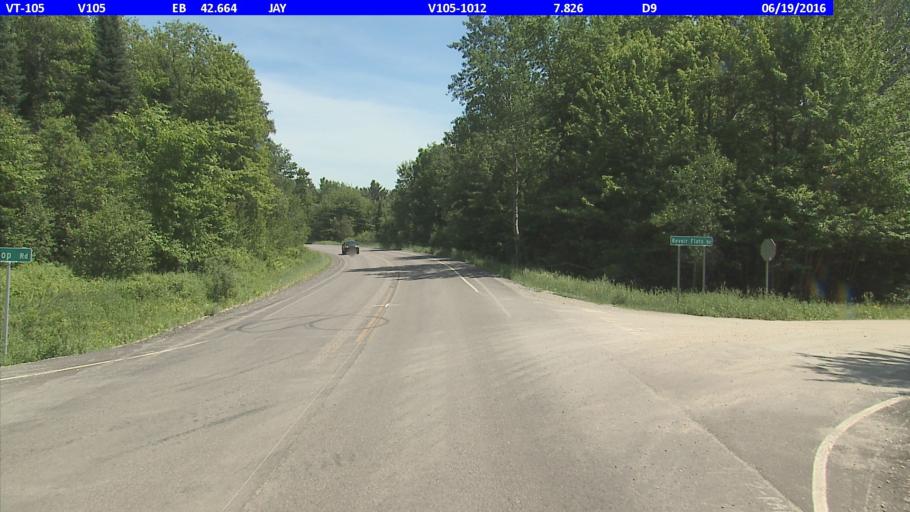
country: CA
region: Quebec
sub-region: Monteregie
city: Sutton
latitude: 44.9649
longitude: -72.4332
